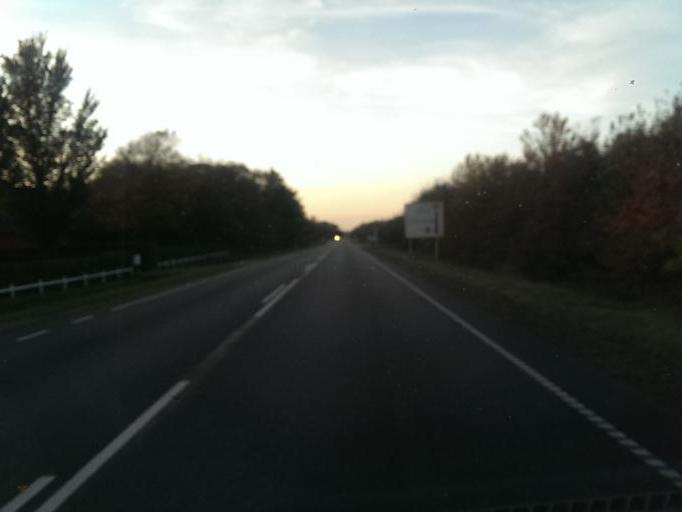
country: DK
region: South Denmark
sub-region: Esbjerg Kommune
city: Bramming
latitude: 55.4765
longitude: 8.6555
